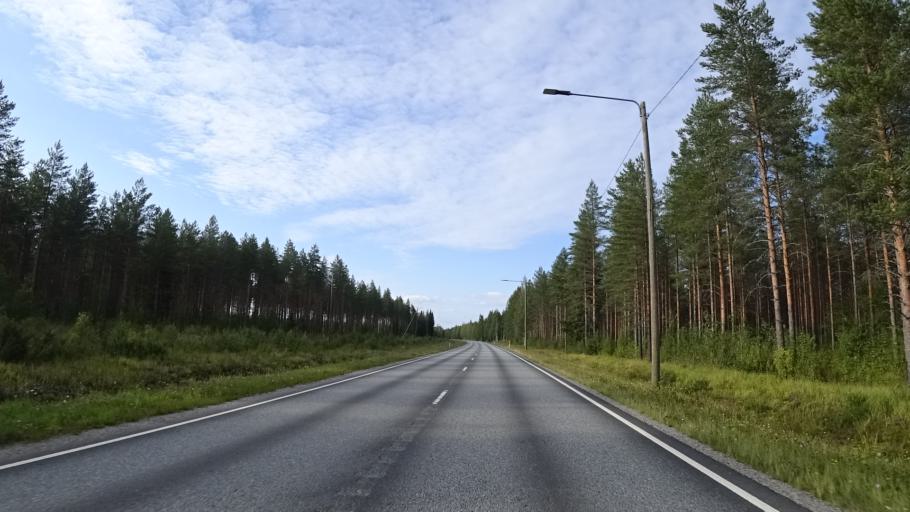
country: FI
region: North Karelia
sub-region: Joensuu
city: Eno
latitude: 62.8742
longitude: 30.2025
